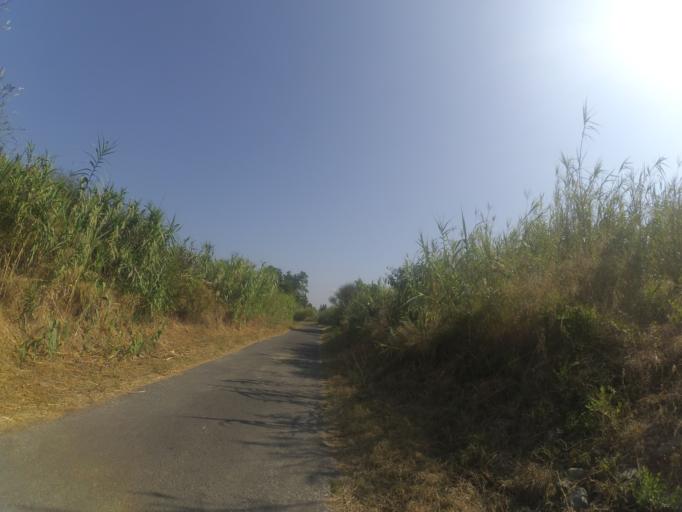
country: FR
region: Languedoc-Roussillon
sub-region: Departement des Pyrenees-Orientales
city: Ille-sur-Tet
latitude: 42.6599
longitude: 2.6252
